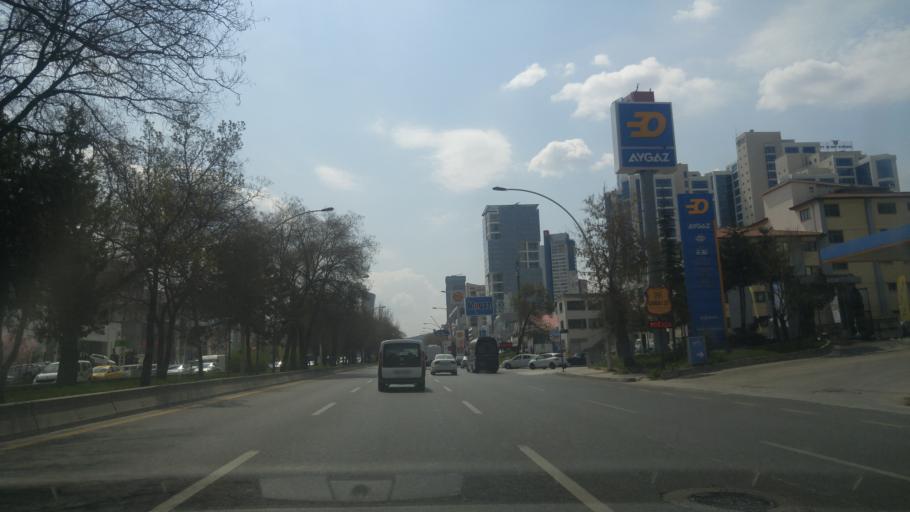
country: TR
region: Ankara
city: Ankara
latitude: 39.8951
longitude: 32.8132
